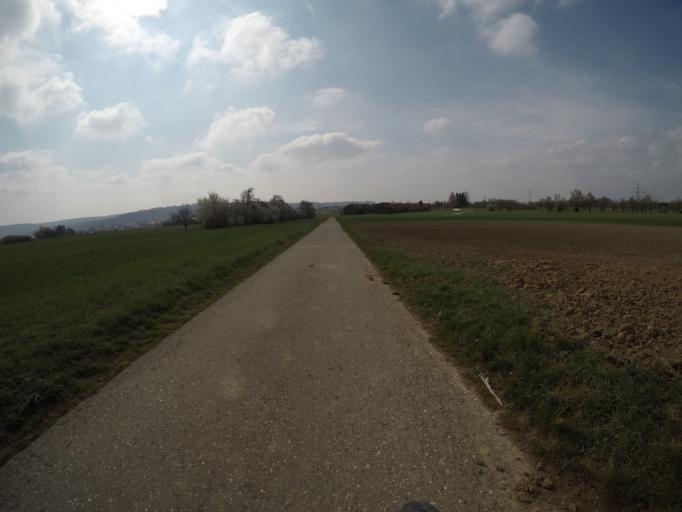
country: DE
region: Baden-Wuerttemberg
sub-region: Regierungsbezirk Stuttgart
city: Nufringen
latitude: 48.6324
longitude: 8.8806
